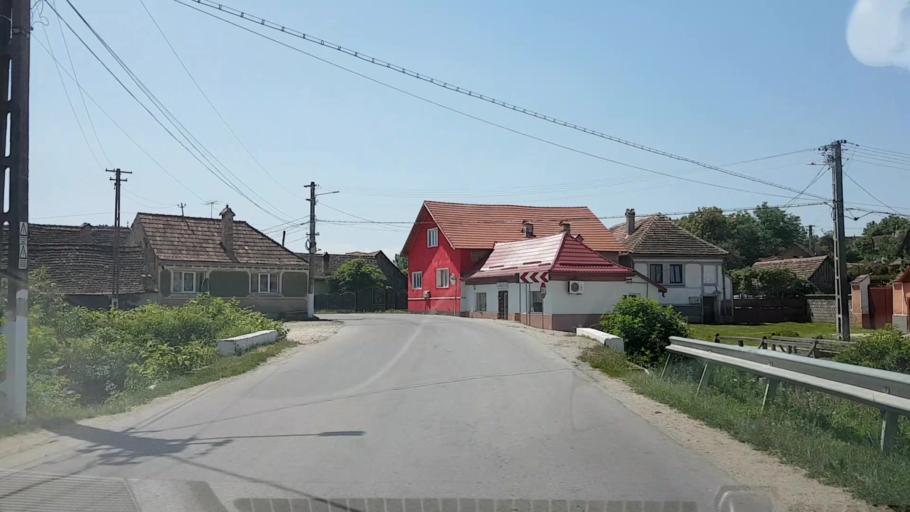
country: RO
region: Brasov
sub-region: Comuna Cincu
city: Cincu
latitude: 45.9132
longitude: 24.8074
